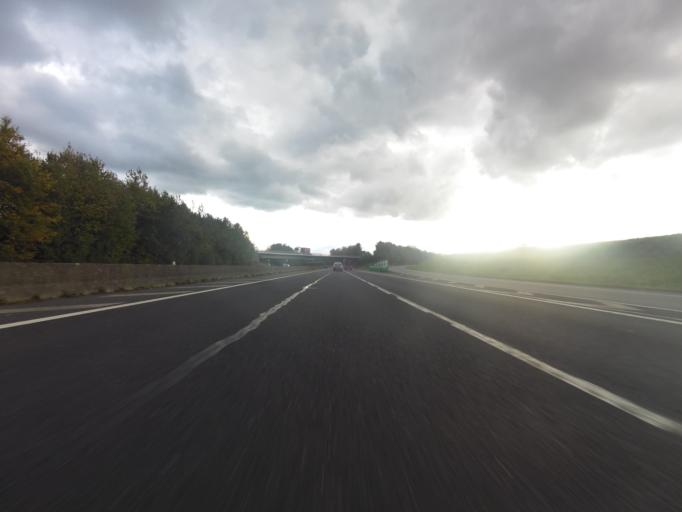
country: FR
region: Haute-Normandie
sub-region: Departement de la Seine-Maritime
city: Saint-Saens
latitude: 49.6520
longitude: 1.2681
